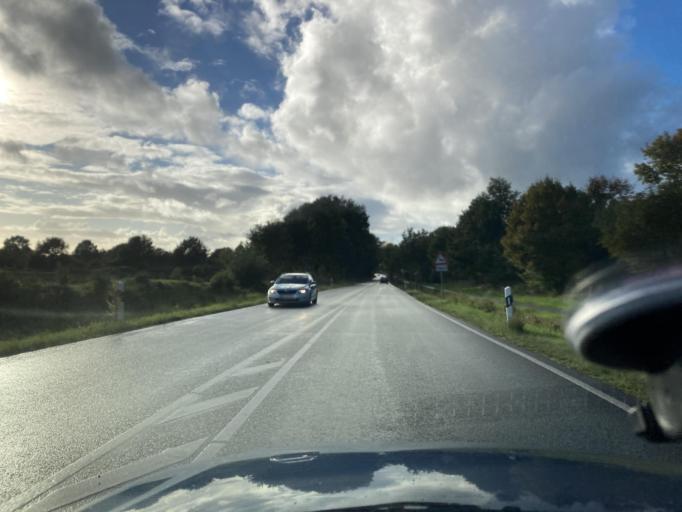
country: DE
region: Schleswig-Holstein
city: Ostrohe
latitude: 54.1970
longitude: 9.1605
